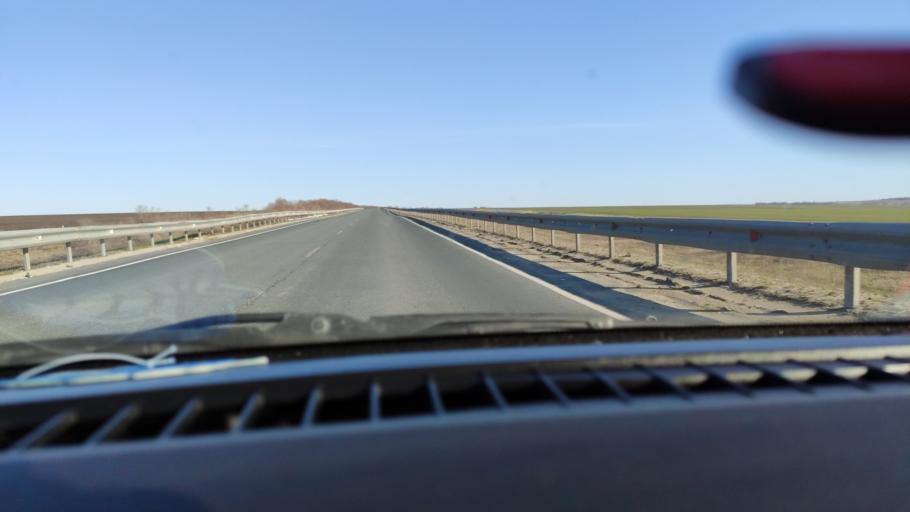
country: RU
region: Saratov
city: Dukhovnitskoye
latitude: 52.7557
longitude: 48.2453
